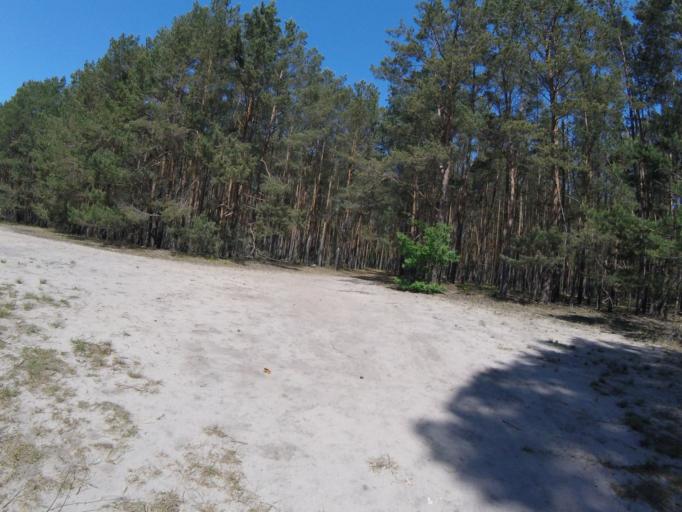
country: DE
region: Brandenburg
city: Bestensee
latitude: 52.2476
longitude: 13.6652
